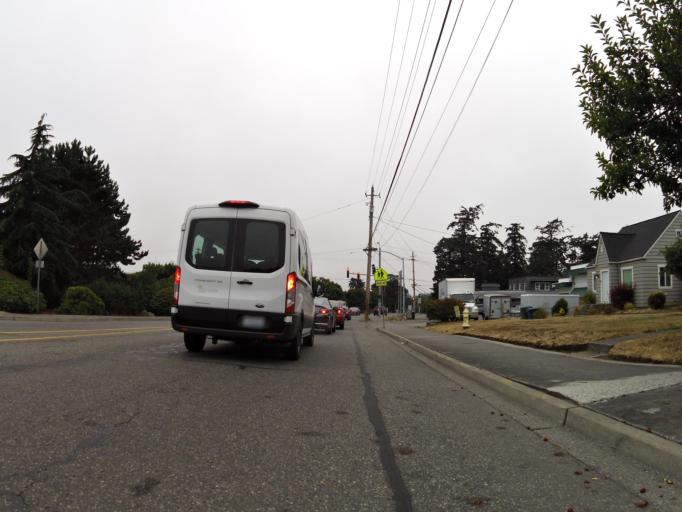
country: US
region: Washington
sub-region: Island County
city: Oak Harbor
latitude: 48.2982
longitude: -122.6423
